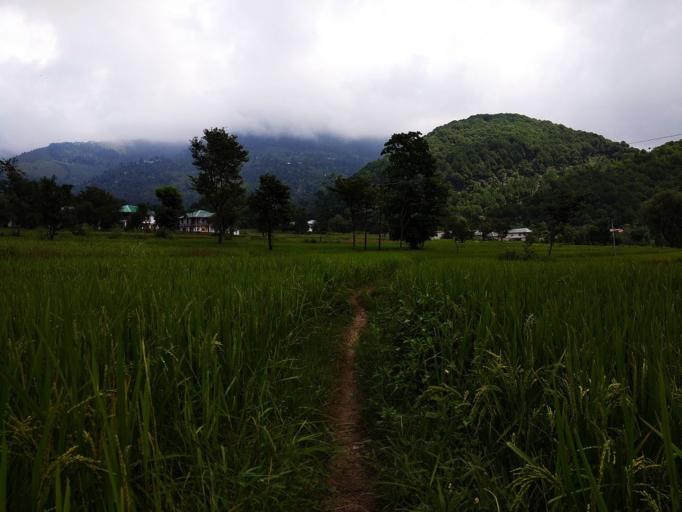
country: IN
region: Himachal Pradesh
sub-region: Kangra
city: Palampur
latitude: 32.1296
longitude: 76.5372
